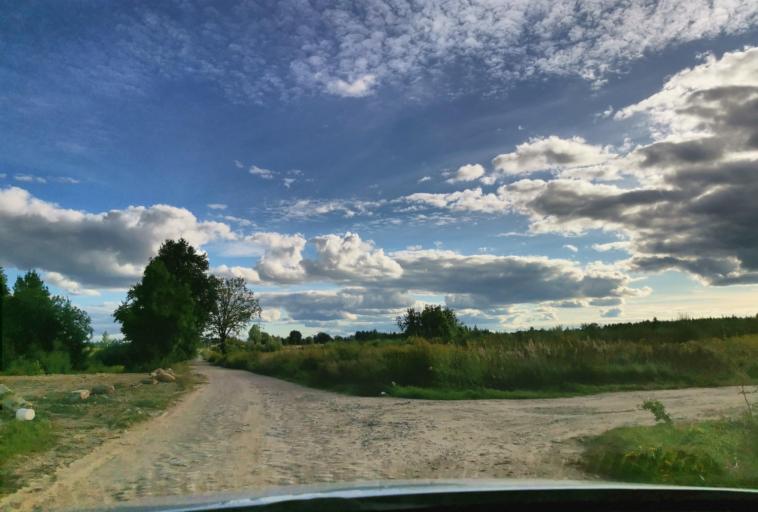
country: RU
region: Kaliningrad
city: Chernyakhovsk
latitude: 54.6366
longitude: 21.7663
